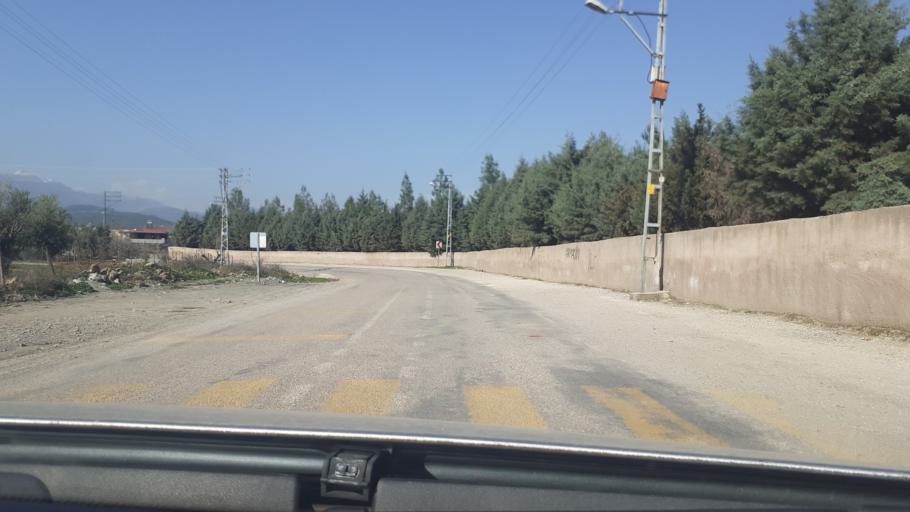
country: TR
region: Hatay
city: Aktepe
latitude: 36.7078
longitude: 36.4873
